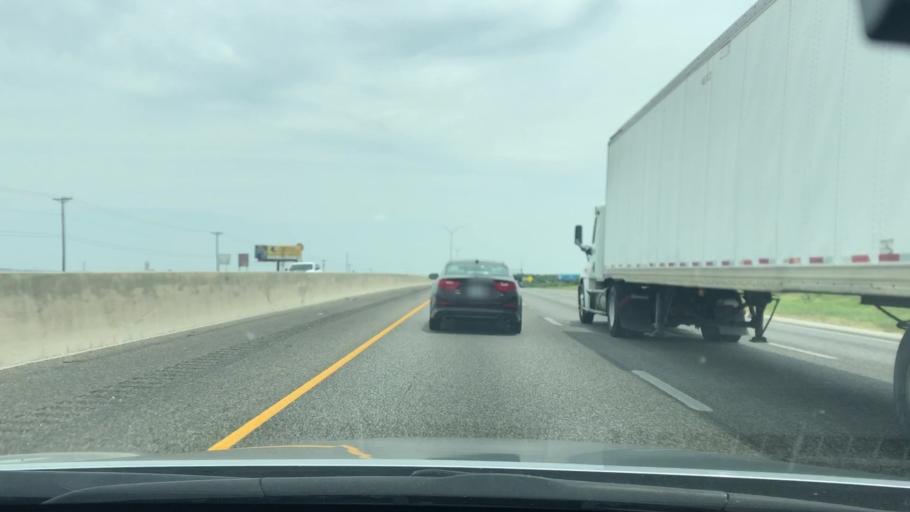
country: US
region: Texas
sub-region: Guadalupe County
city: Northcliff
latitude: 29.6361
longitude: -98.2187
